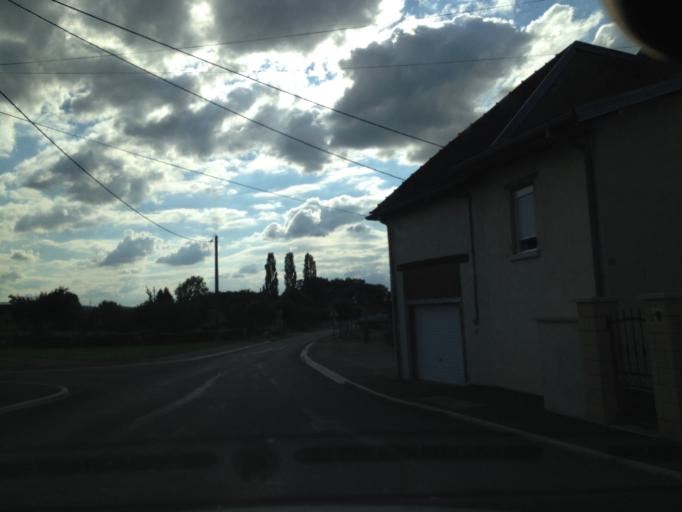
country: FR
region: Franche-Comte
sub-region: Departement de la Haute-Saone
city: Faverney
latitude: 47.7868
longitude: 6.0067
